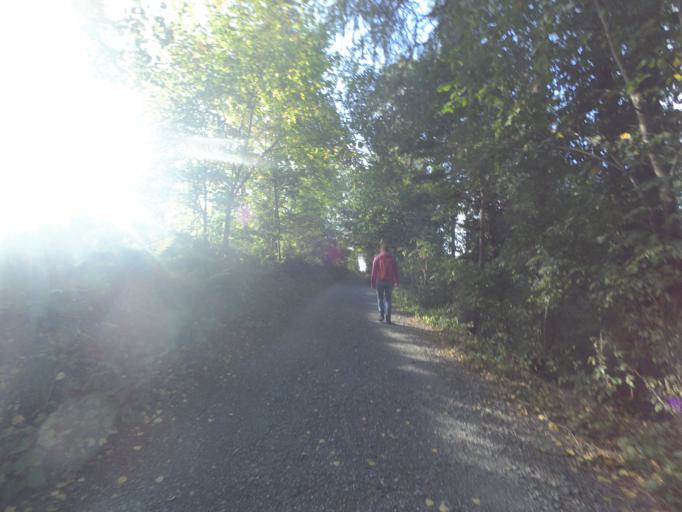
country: AT
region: Styria
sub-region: Politischer Bezirk Leibnitz
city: Kitzeck im Sausal
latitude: 46.7880
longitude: 15.4281
